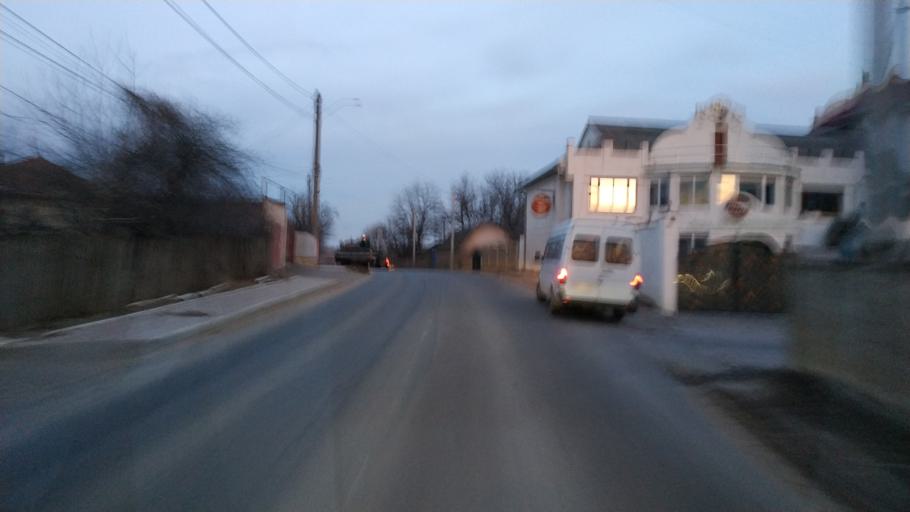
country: MD
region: Laloveni
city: Ialoveni
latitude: 46.9398
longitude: 28.7890
